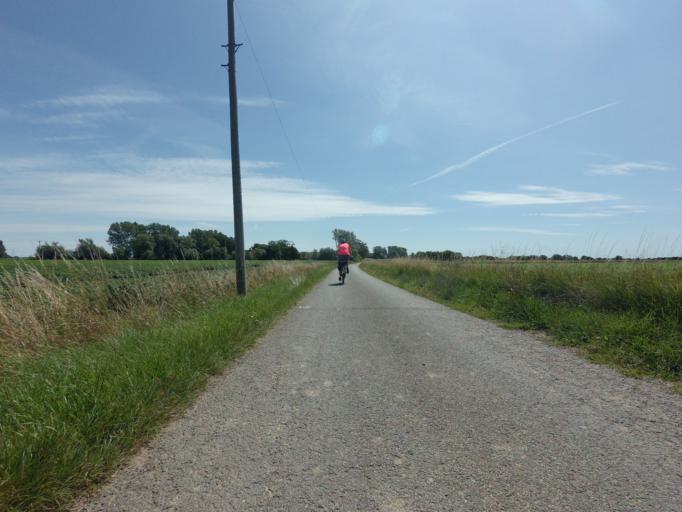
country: GB
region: England
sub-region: Kent
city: Lydd
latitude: 50.9827
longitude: 0.8786
